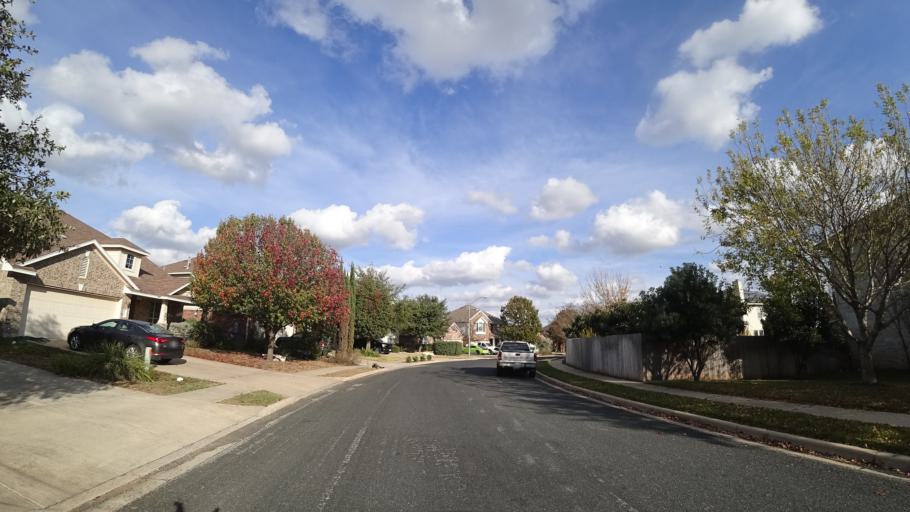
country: US
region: Texas
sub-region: Williamson County
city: Brushy Creek
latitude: 30.5074
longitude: -97.7261
